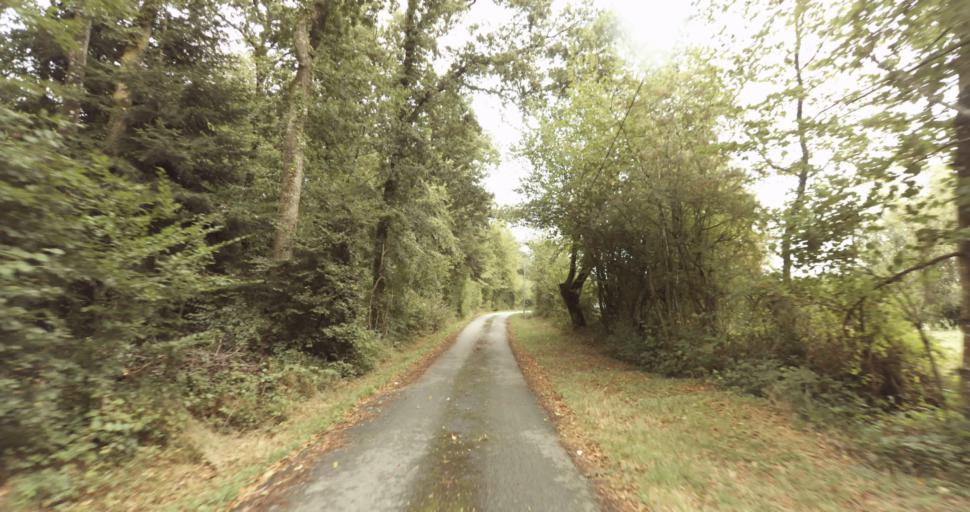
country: FR
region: Lower Normandy
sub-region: Departement de l'Orne
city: Sainte-Gauburge-Sainte-Colombe
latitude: 48.7523
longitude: 0.3881
